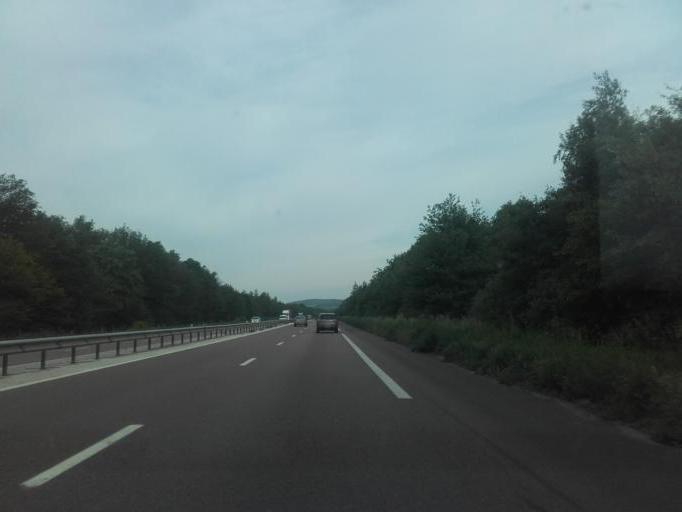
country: FR
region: Bourgogne
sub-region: Departement de Saone-et-Loire
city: Givry
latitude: 46.7584
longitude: 4.7697
